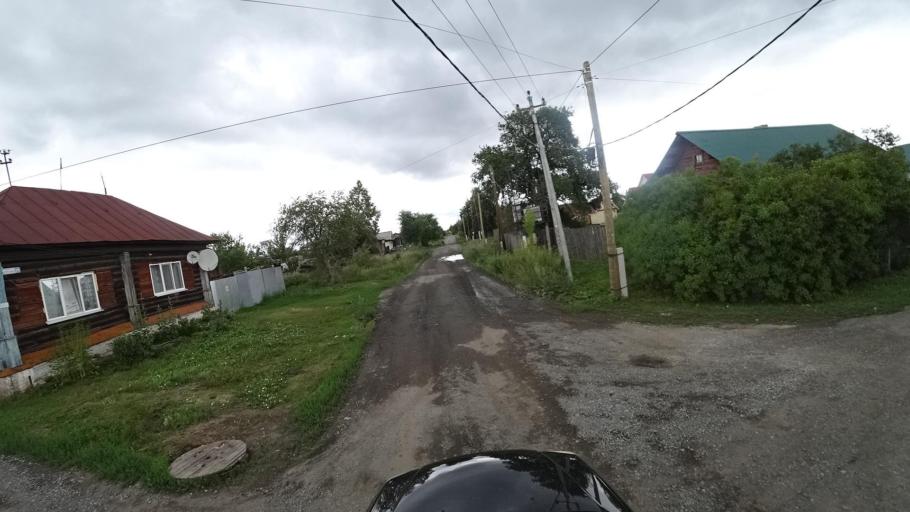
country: RU
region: Sverdlovsk
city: Kamyshlov
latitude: 56.8530
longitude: 62.6882
